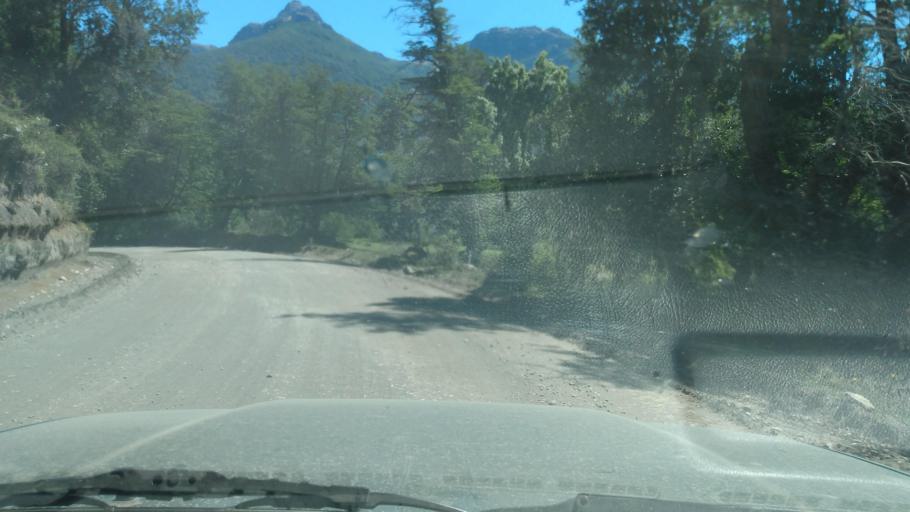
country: AR
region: Neuquen
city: Villa La Angostura
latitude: -40.6205
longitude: -71.5788
